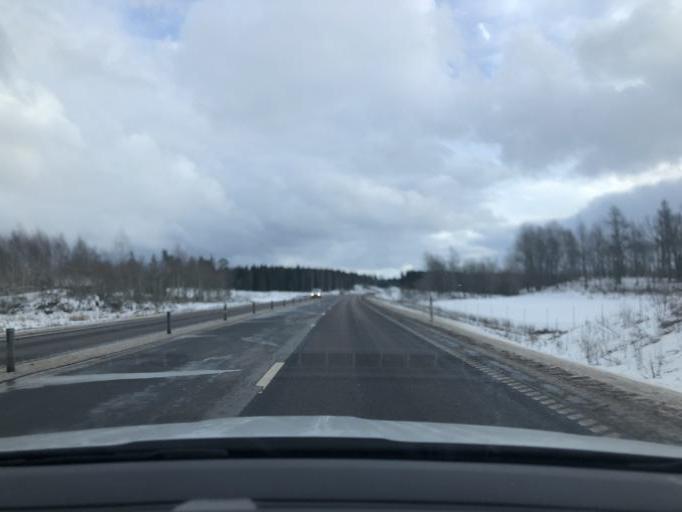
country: SE
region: OEstergoetland
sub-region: Motala Kommun
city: Borensberg
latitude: 58.5890
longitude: 15.1812
